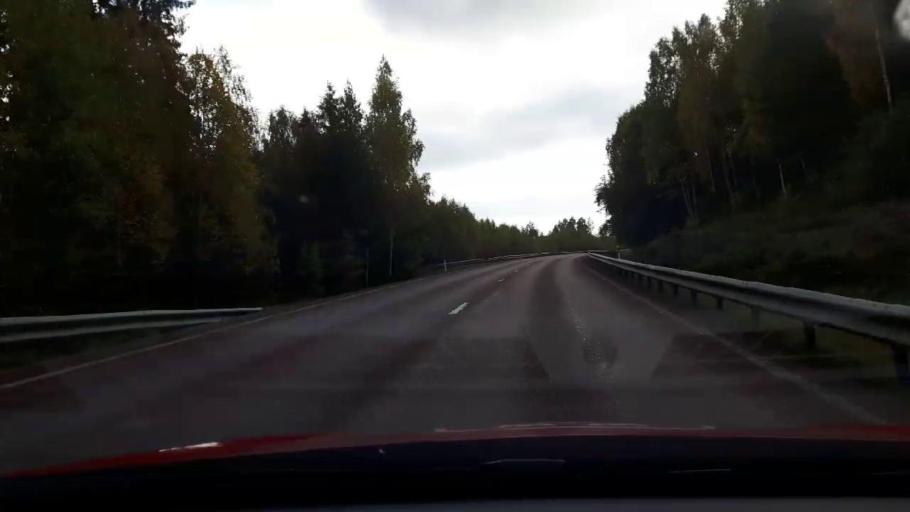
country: SE
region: Gaevleborg
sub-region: Ljusdals Kommun
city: Jaervsoe
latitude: 61.6175
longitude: 16.2934
